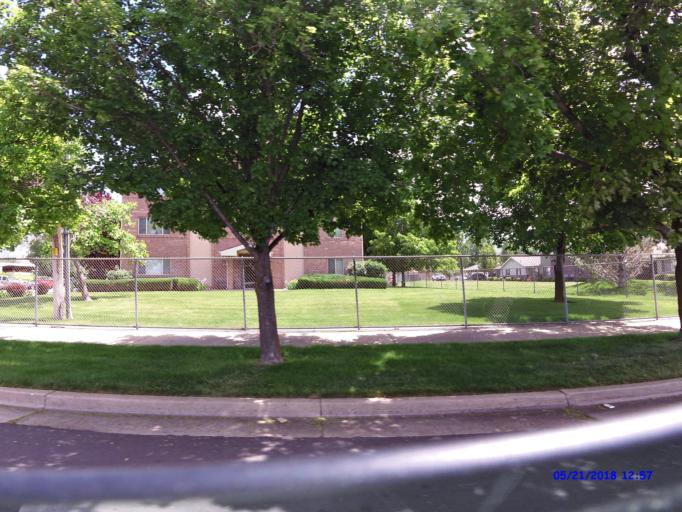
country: US
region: Utah
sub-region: Weber County
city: South Ogden
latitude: 41.2068
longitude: -111.9764
